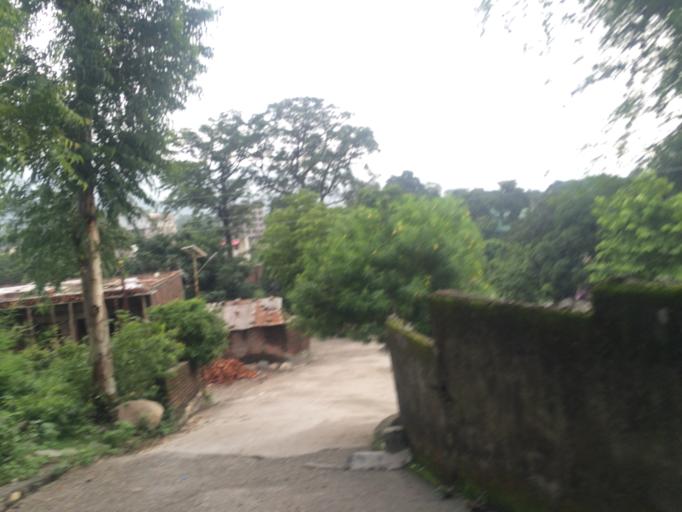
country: IN
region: Uttarakhand
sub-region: Dehradun
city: Birbhaddar
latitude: 30.0743
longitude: 78.2782
